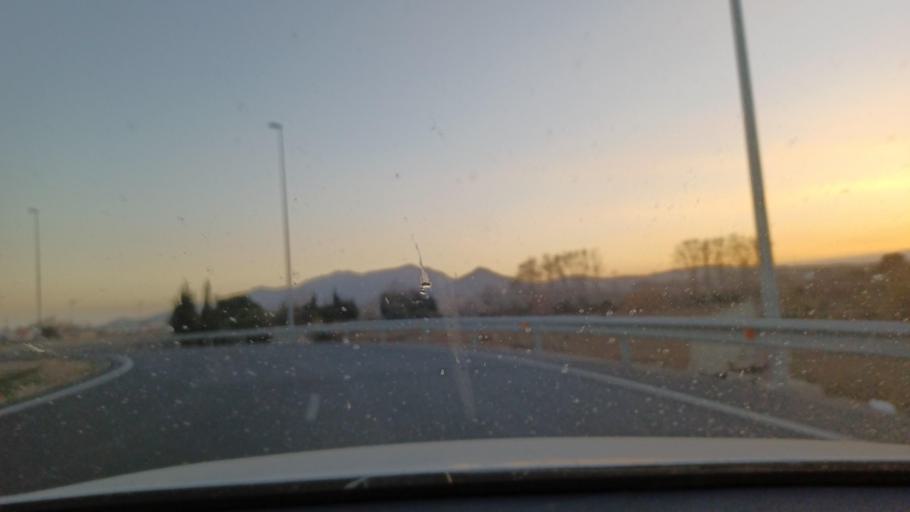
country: ES
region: Catalonia
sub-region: Provincia de Tarragona
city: Amposta
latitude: 40.7223
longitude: 0.5886
